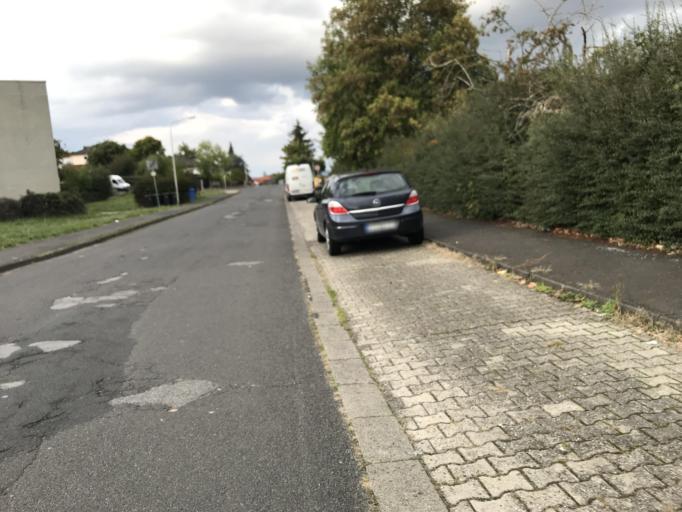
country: DE
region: Hesse
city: Borken
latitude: 51.0381
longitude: 9.2890
